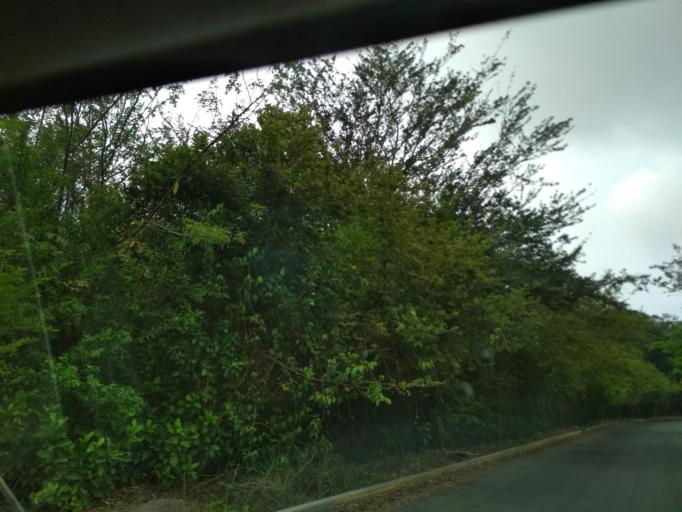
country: MX
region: Veracruz
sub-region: Medellin
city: Fraccionamiento Arboledas San Ramon
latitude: 19.0909
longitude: -96.1427
